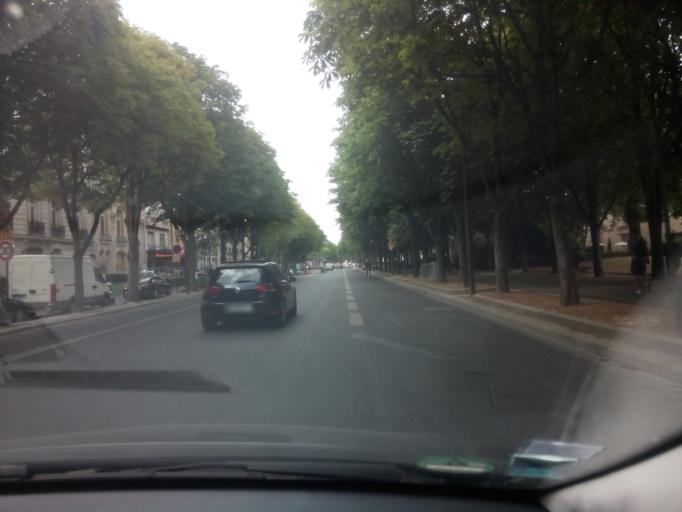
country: FR
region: Ile-de-France
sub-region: Departement des Hauts-de-Seine
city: Clichy
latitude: 48.8665
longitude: 2.3104
